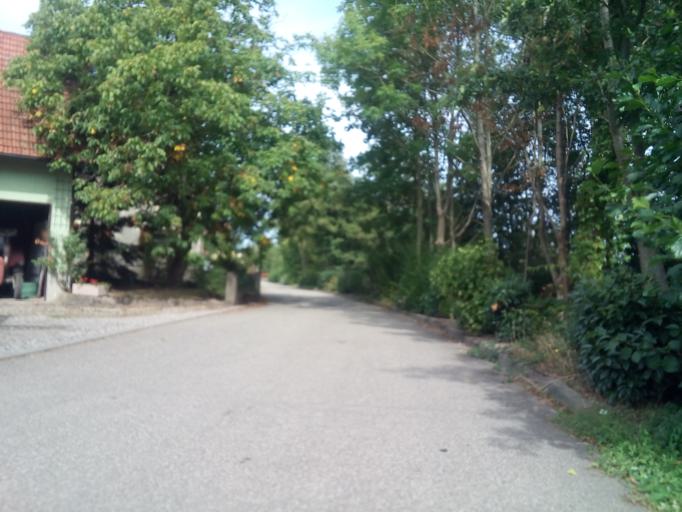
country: DE
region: Baden-Wuerttemberg
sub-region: Karlsruhe Region
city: Zell
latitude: 48.7163
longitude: 8.0672
